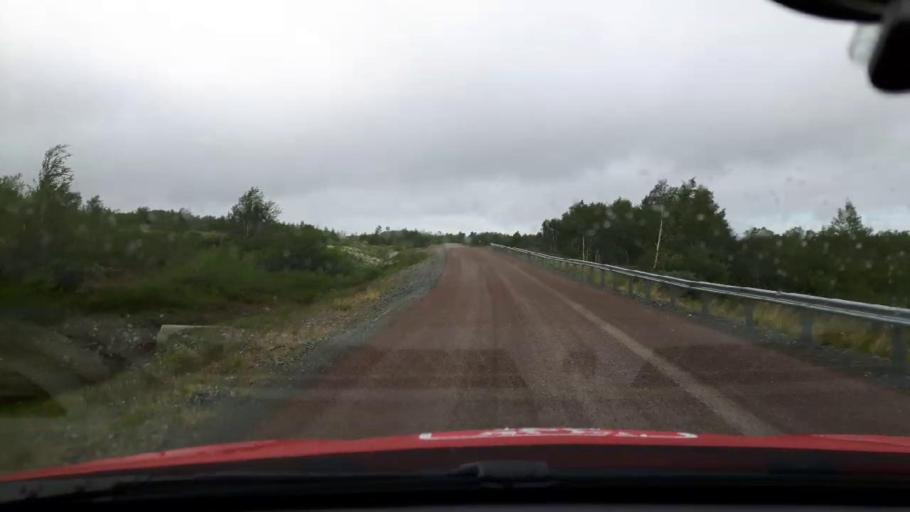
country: NO
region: Nord-Trondelag
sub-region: Meraker
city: Meraker
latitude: 63.2100
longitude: 12.4041
